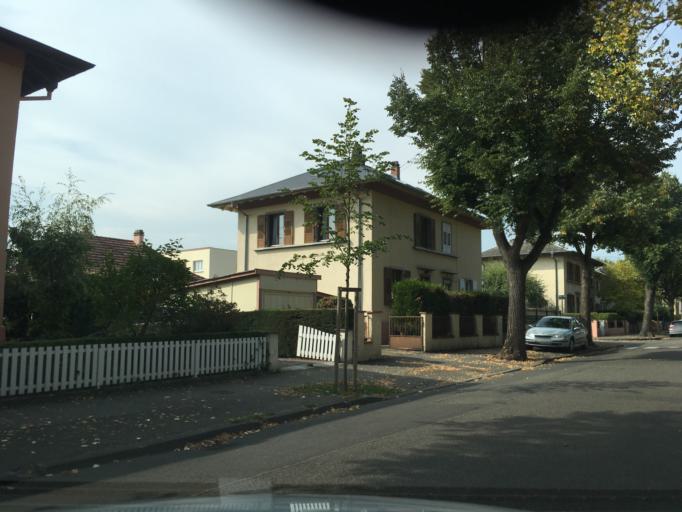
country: FR
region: Alsace
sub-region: Departement du Haut-Rhin
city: Colmar
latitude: 48.0865
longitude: 7.3703
